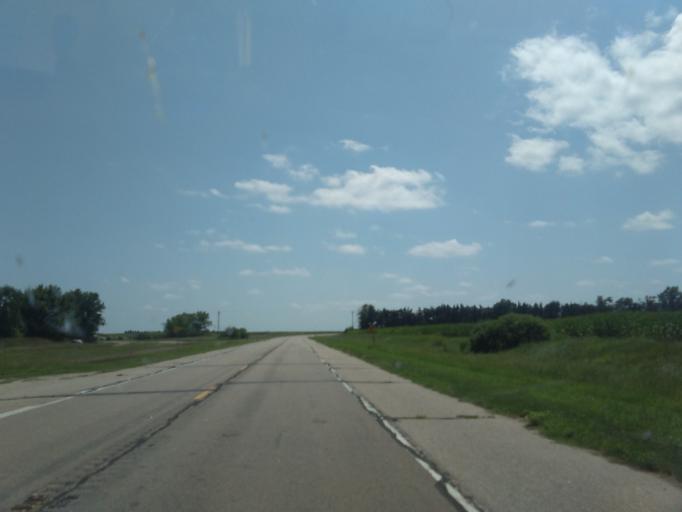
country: US
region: Nebraska
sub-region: Dawson County
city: Lexington
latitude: 40.6923
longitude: -99.7946
